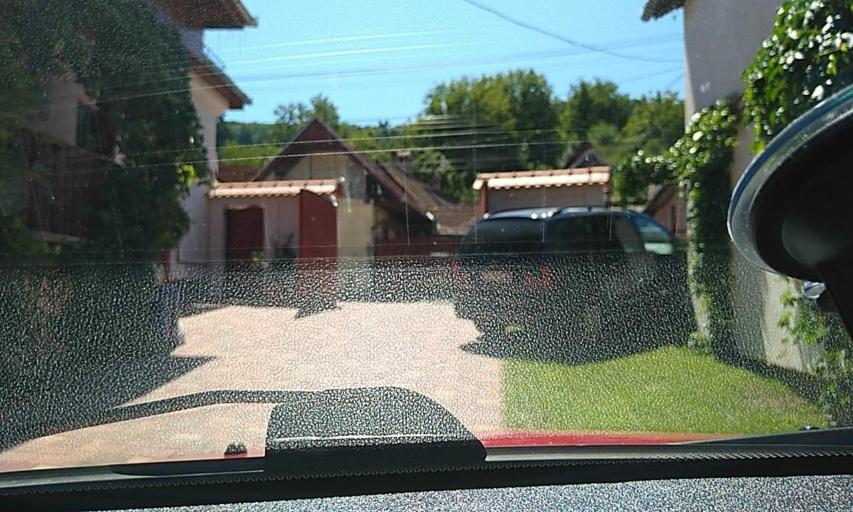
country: RO
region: Mures
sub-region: Municipiul Sighisoara
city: Sighisoara
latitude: 46.2142
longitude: 24.7905
